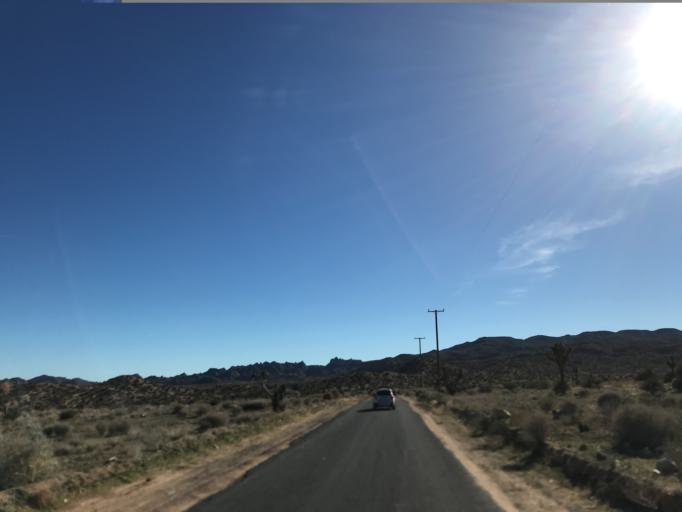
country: US
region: California
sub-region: San Bernardino County
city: Yucca Valley
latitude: 34.1944
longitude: -116.5461
